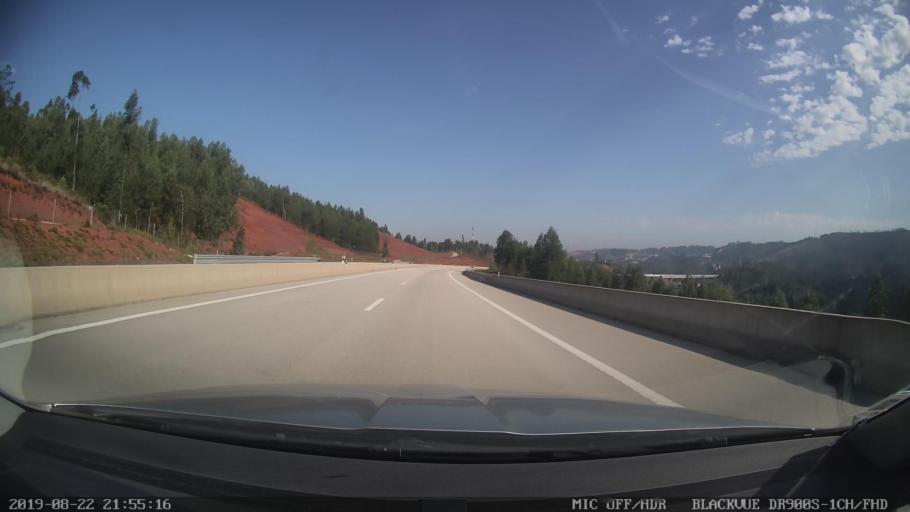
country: PT
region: Coimbra
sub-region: Coimbra
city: Coimbra
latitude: 40.1506
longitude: -8.3843
